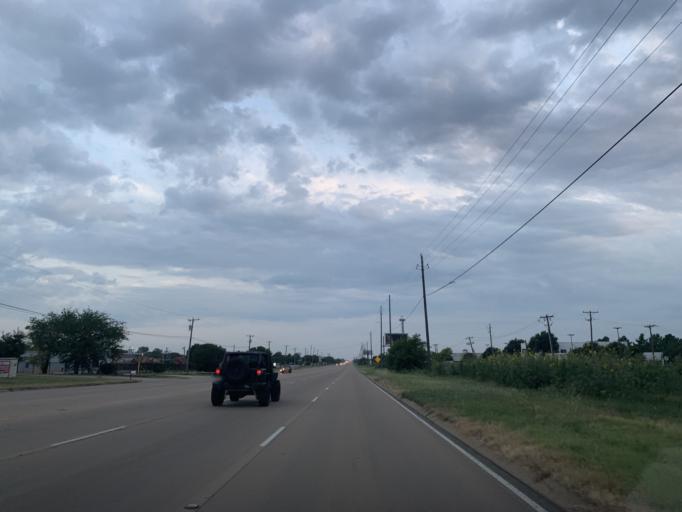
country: US
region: Texas
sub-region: Tarrant County
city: Keller
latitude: 32.9101
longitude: -97.2563
